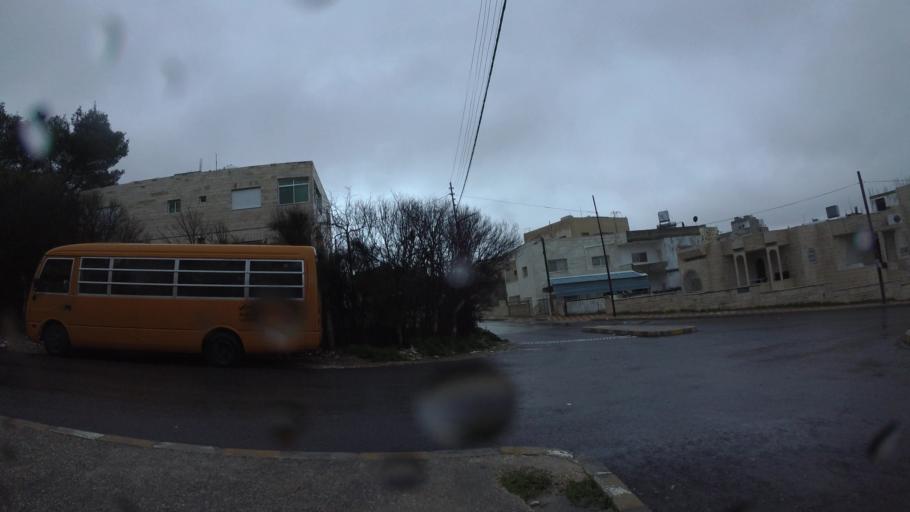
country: JO
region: Amman
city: Al Jubayhah
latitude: 32.0288
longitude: 35.8457
